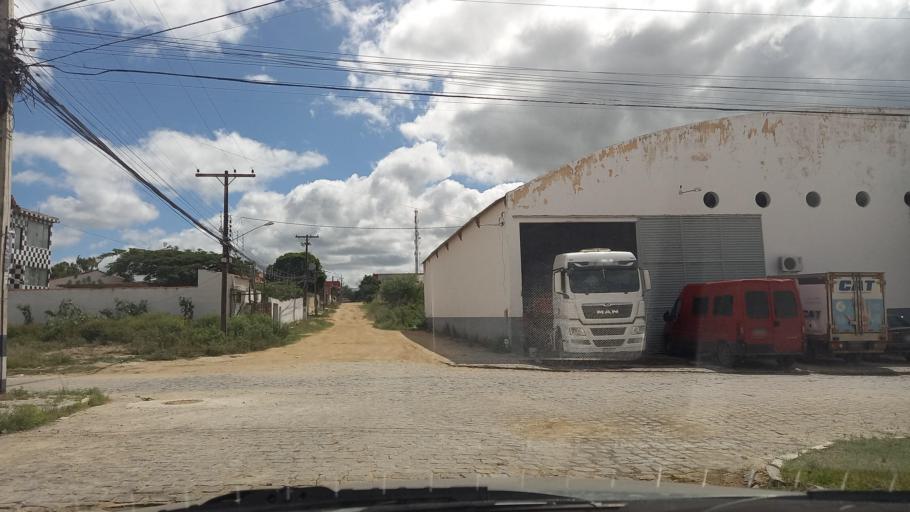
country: BR
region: Pernambuco
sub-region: Caruaru
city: Caruaru
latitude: -8.2574
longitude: -35.9774
